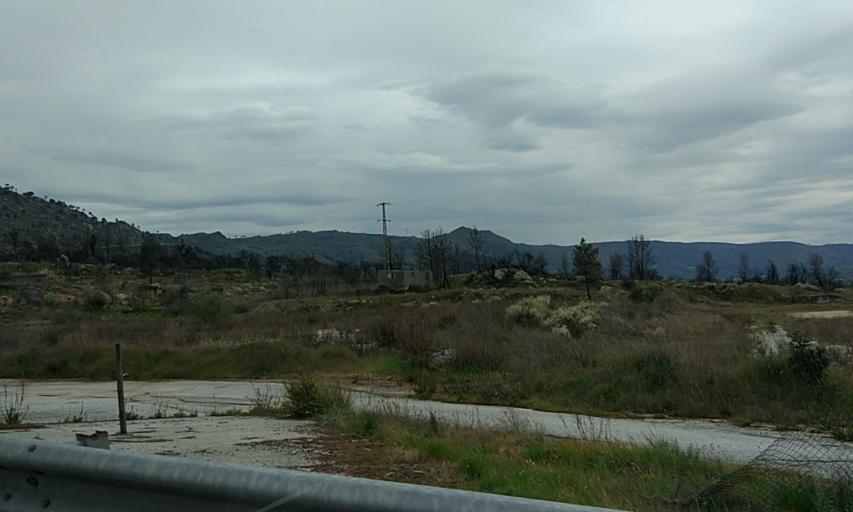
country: PT
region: Guarda
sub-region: Guarda
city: Guarda
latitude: 40.6212
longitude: -7.2912
